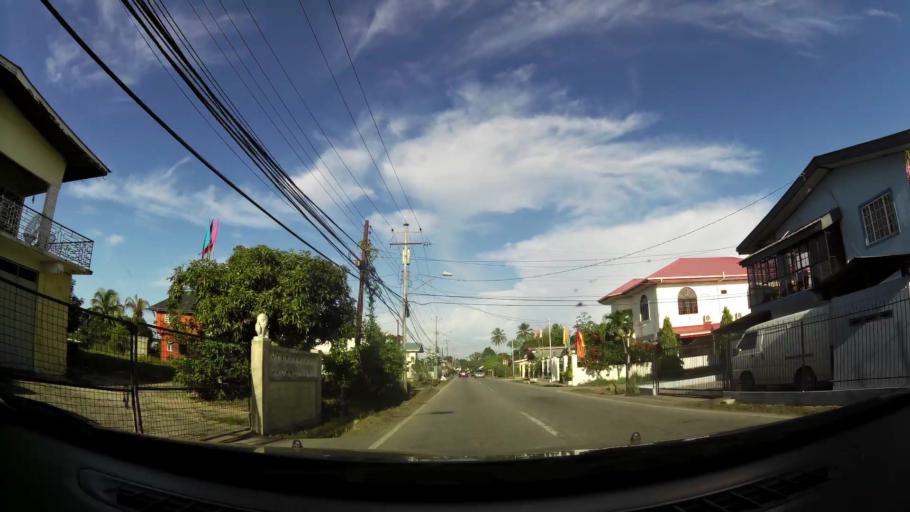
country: TT
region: Chaguanas
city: Chaguanas
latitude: 10.5489
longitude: -61.3567
